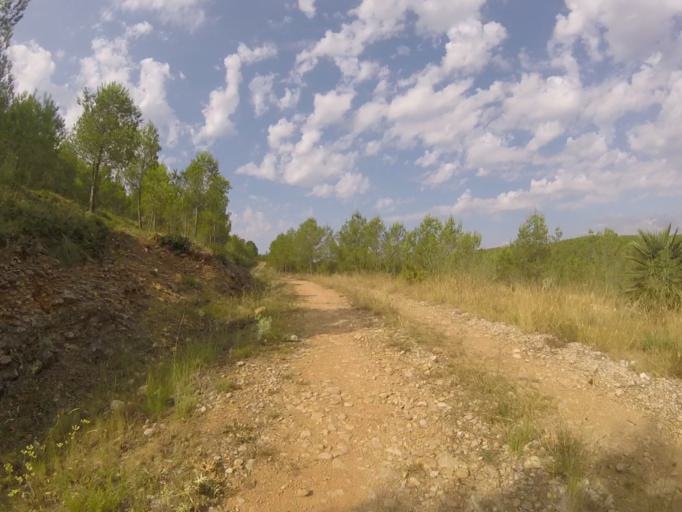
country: ES
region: Valencia
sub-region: Provincia de Castello
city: Alcala de Xivert
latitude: 40.3658
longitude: 0.2043
